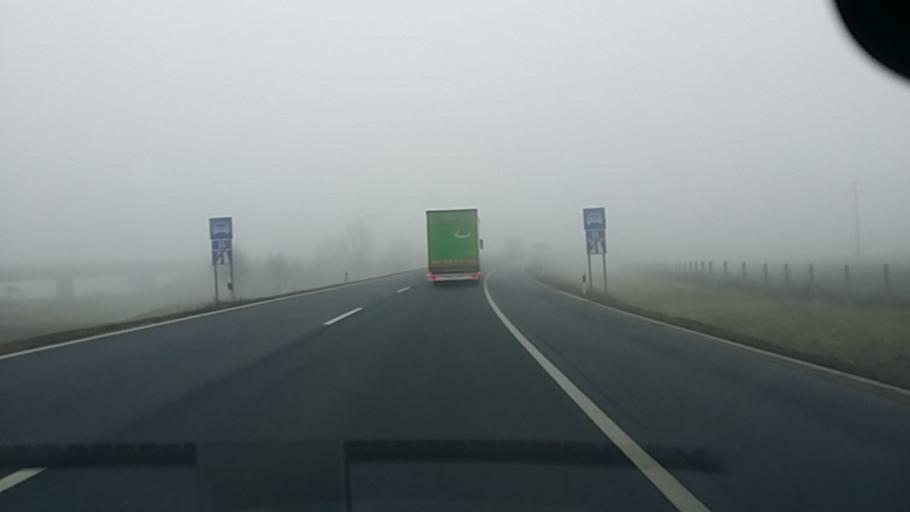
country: HU
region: Gyor-Moson-Sopron
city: Mosonmagyarovar
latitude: 47.8908
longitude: 17.1829
